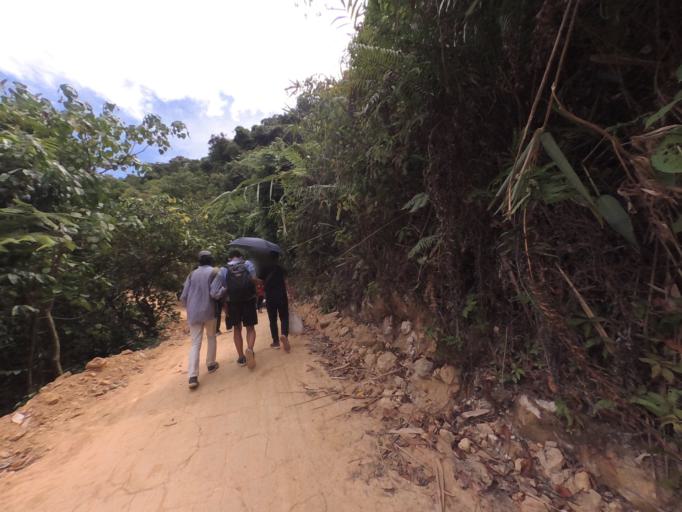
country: VN
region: Thua Thien-Hue
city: A Luoi
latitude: 16.3076
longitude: 107.2170
